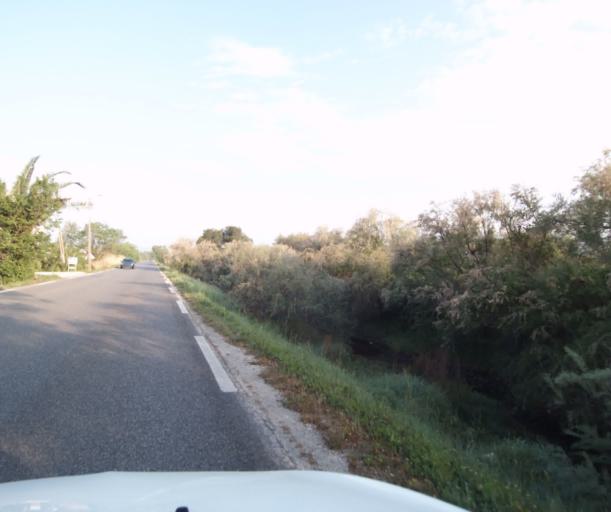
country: FR
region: Provence-Alpes-Cote d'Azur
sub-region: Departement du Var
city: La Londe-les-Maures
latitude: 43.1152
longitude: 6.1922
